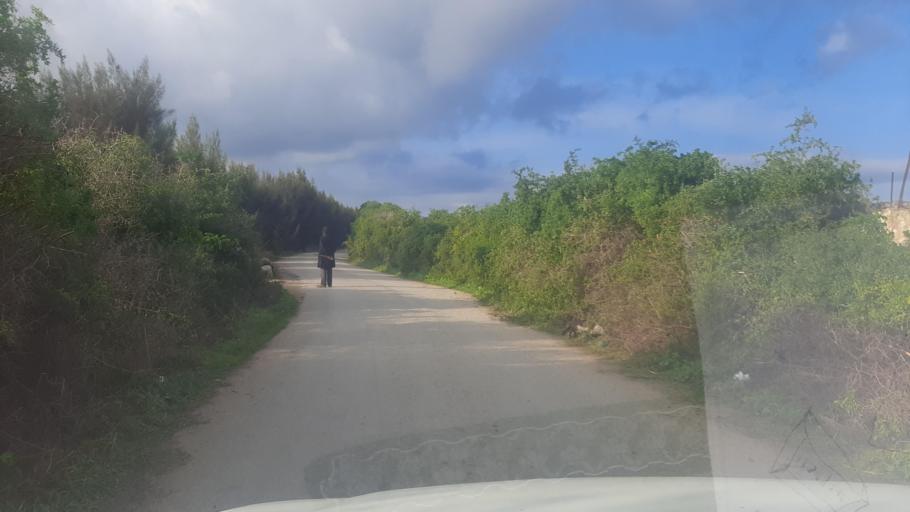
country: TN
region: Nabul
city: Manzil Bu Zalafah
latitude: 36.7089
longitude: 10.5019
